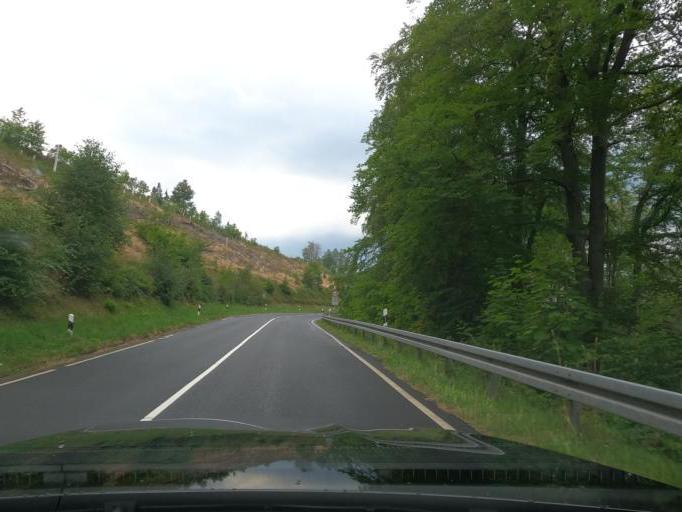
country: DE
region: Lower Saxony
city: Goslar
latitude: 51.8727
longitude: 10.3876
